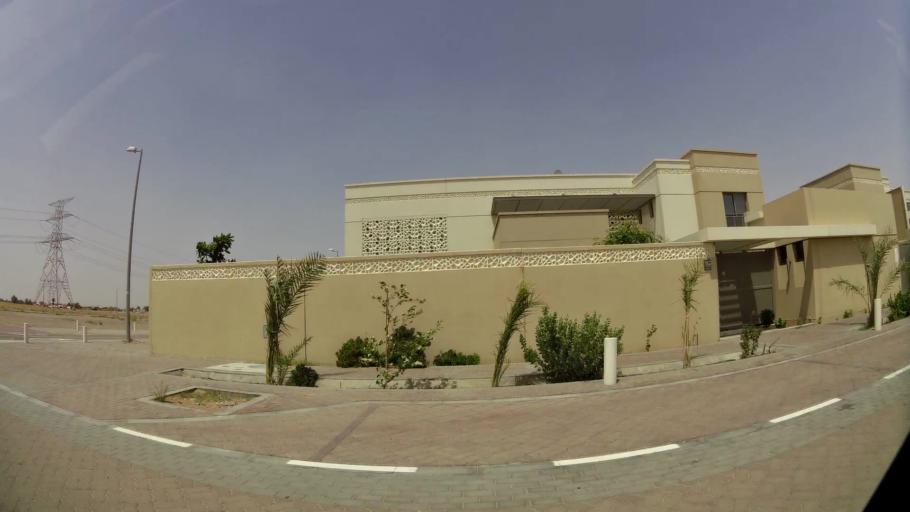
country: AE
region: Abu Dhabi
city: Al Ain
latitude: 24.1458
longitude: 55.6206
